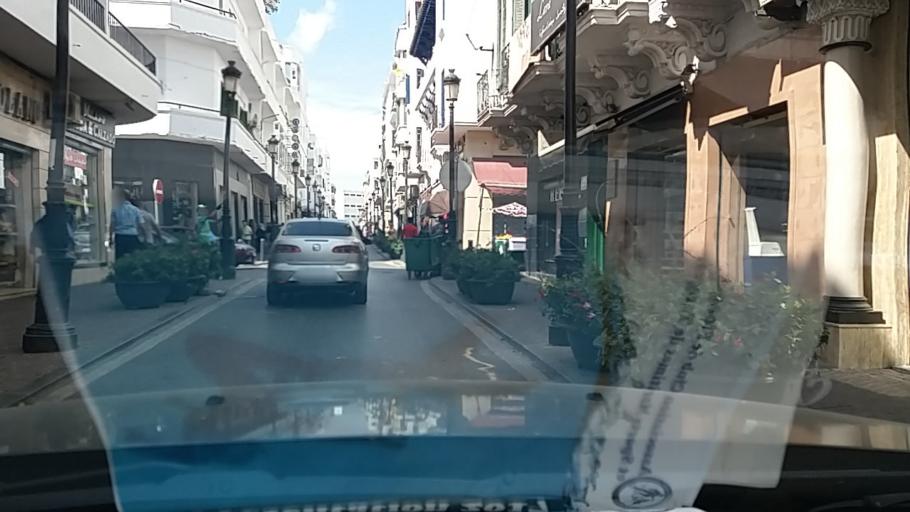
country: MA
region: Tanger-Tetouan
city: Tetouan
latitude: 35.5714
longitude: -5.3749
